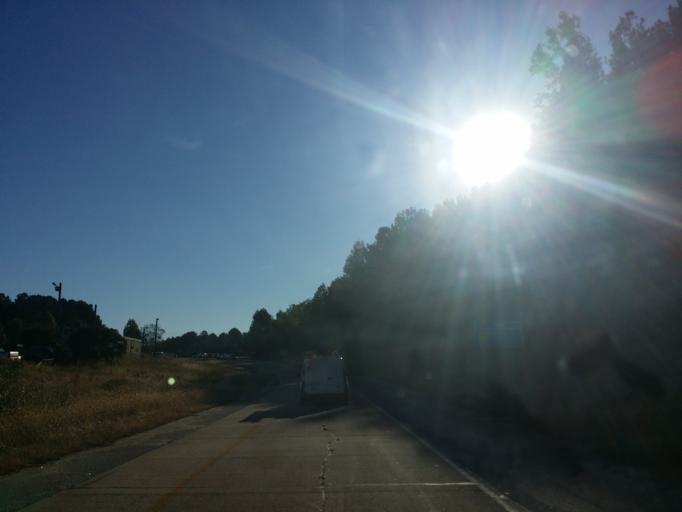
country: US
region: North Carolina
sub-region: Wake County
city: West Raleigh
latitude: 35.7562
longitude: -78.6688
